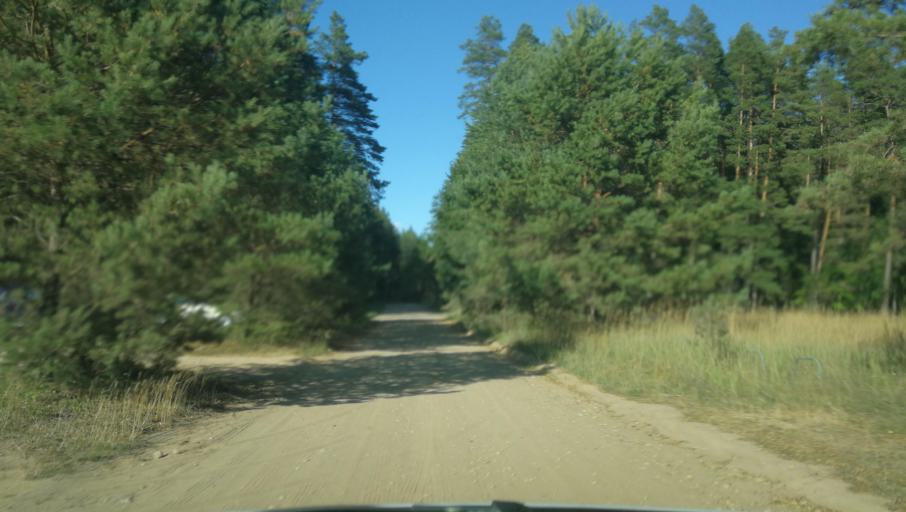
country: LV
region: Cesu Rajons
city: Cesis
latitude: 57.2760
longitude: 25.1998
